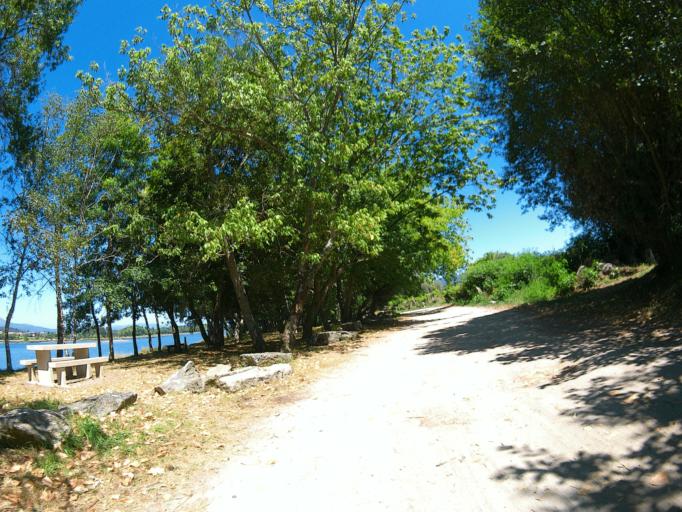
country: PT
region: Viana do Castelo
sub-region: Viana do Castelo
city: Darque
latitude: 41.6983
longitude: -8.7462
